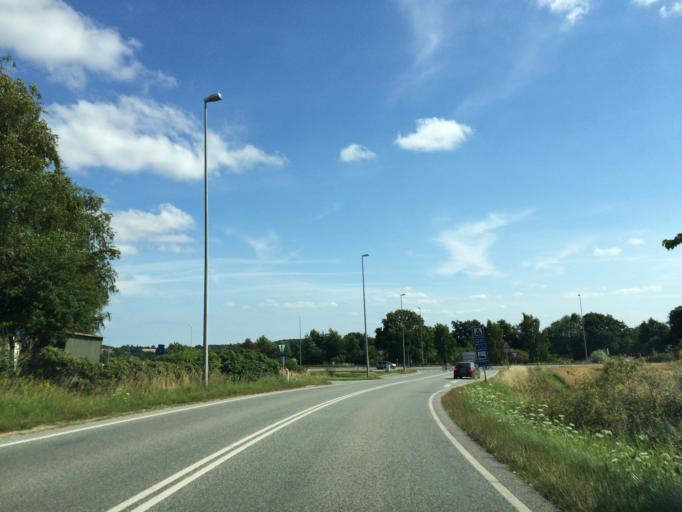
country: DK
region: Central Jutland
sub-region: Syddjurs Kommune
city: Ronde
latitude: 56.3066
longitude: 10.4485
